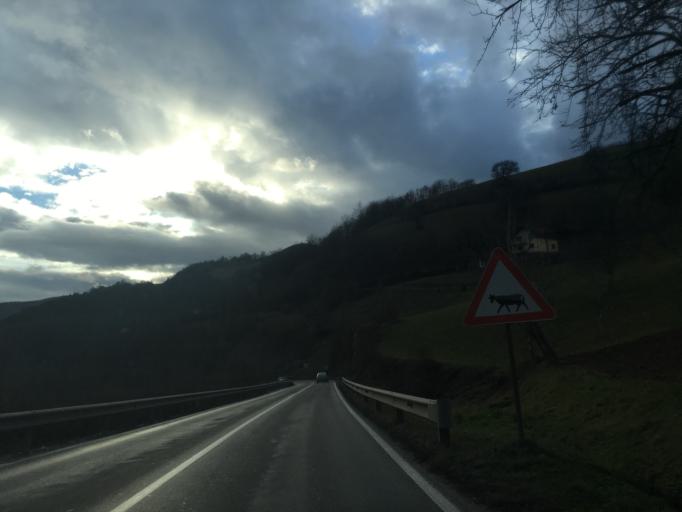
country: RS
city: Sokolovo Brdo
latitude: 43.1406
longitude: 19.7777
